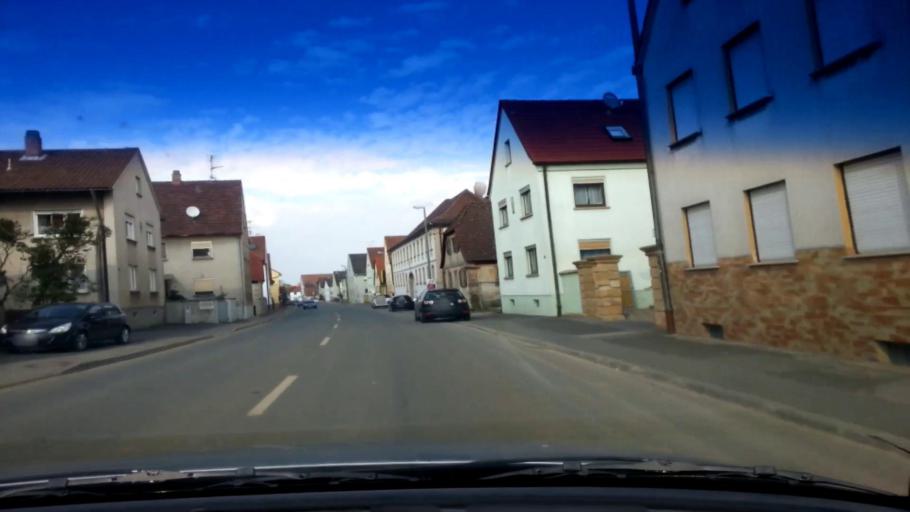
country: DE
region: Bavaria
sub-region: Upper Franconia
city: Breitengussbach
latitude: 49.9685
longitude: 10.8852
